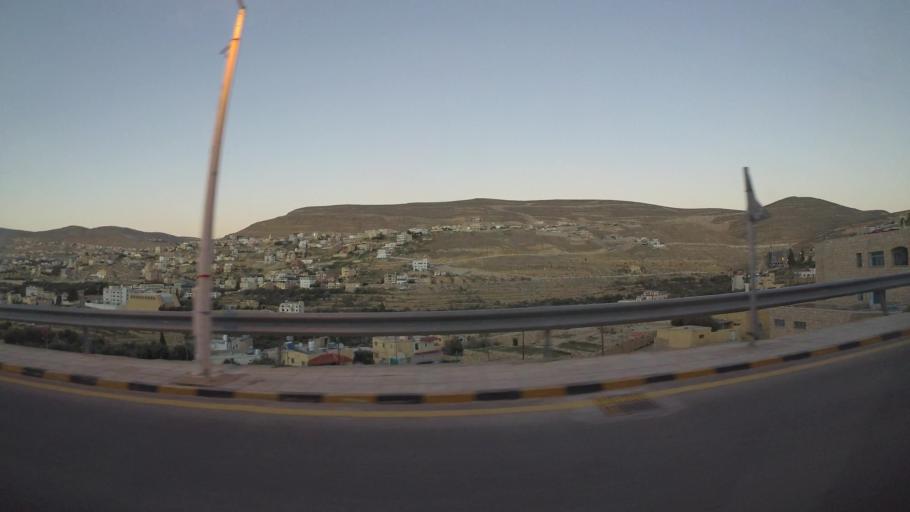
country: JO
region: Ma'an
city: Petra
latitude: 30.3138
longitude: 35.4782
